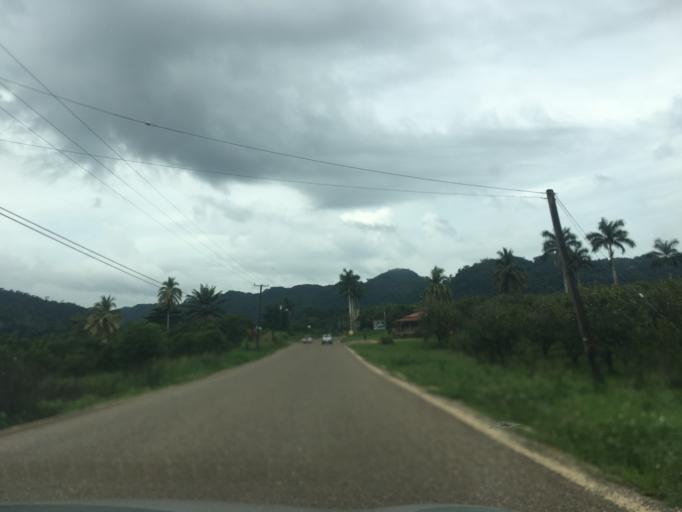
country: BZ
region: Cayo
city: Belmopan
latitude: 17.0967
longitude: -88.6617
